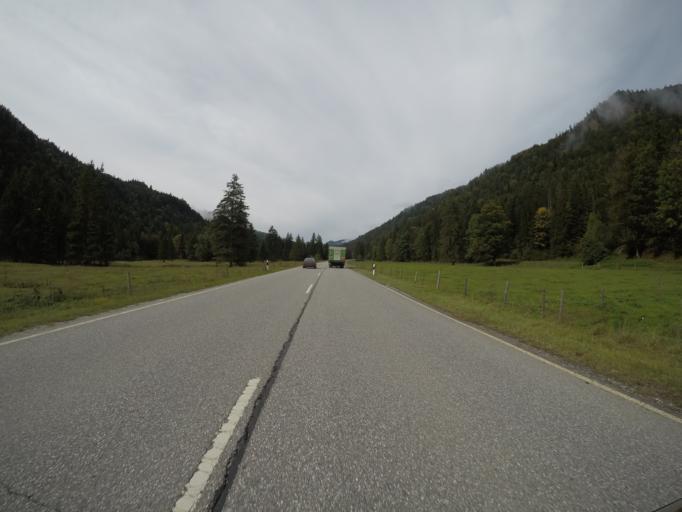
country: DE
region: Bavaria
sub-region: Upper Bavaria
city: Kreuth
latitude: 47.6199
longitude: 11.7038
